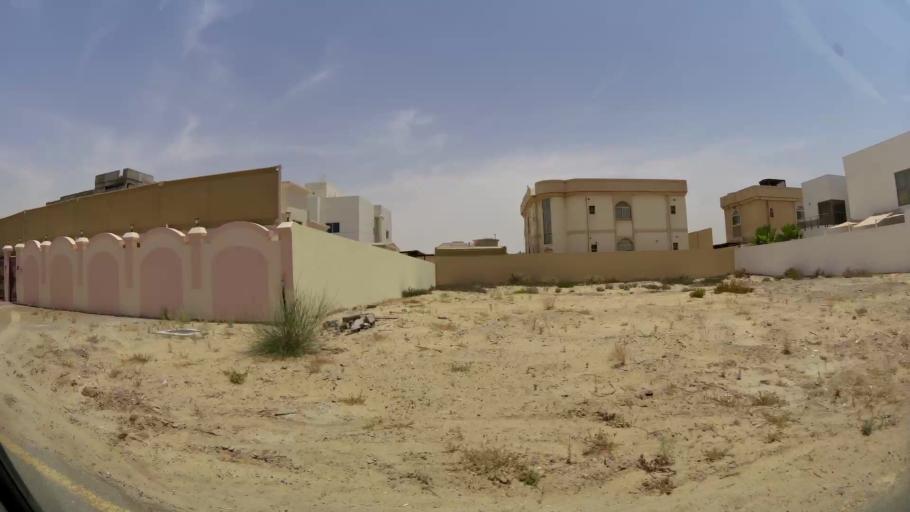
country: AE
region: Ash Shariqah
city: Sharjah
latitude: 25.2438
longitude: 55.4652
